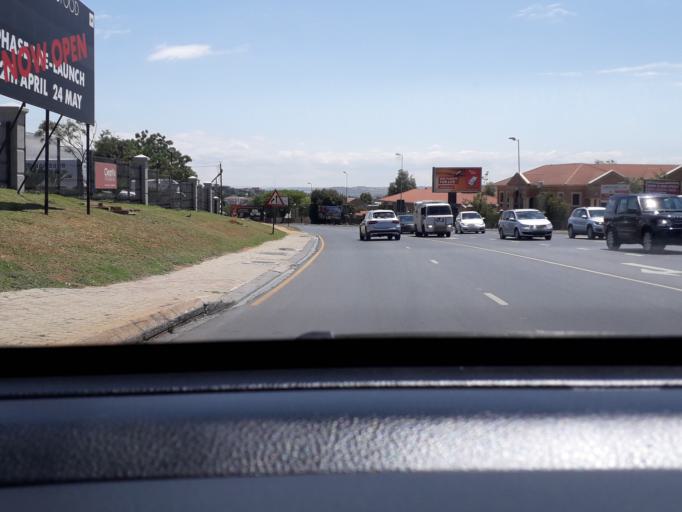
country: ZA
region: Gauteng
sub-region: City of Johannesburg Metropolitan Municipality
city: Modderfontein
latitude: -26.0749
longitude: 28.0651
